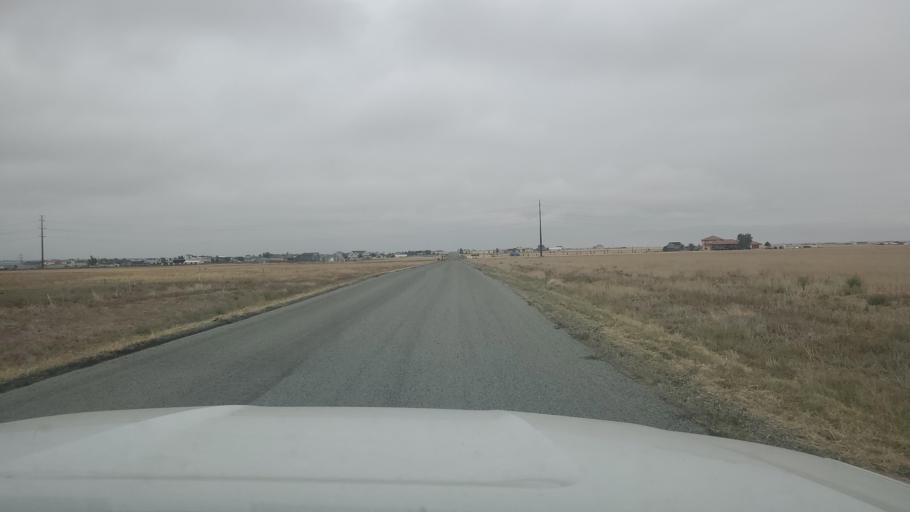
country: US
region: Colorado
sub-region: Weld County
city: Lochbuie
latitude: 39.9390
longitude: -104.6028
